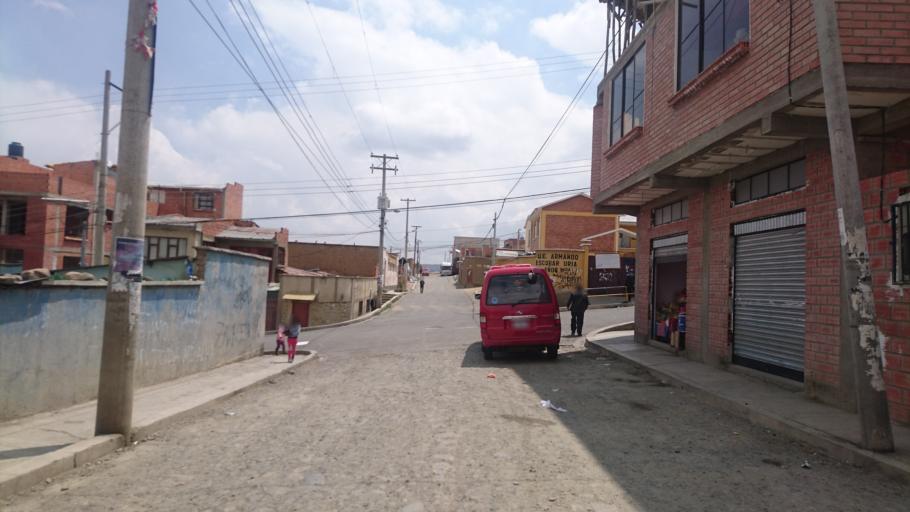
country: BO
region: La Paz
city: La Paz
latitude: -16.4884
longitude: -68.1039
